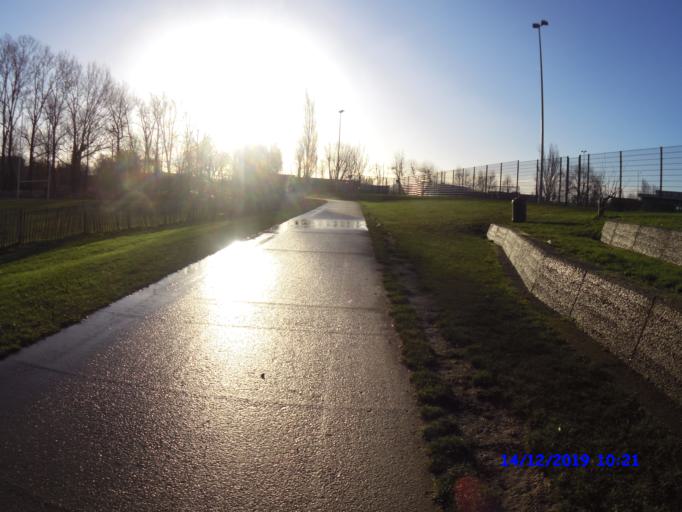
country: BE
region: Flanders
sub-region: Provincie Vlaams-Brabant
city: Drogenbos
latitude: 50.8029
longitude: 4.3115
